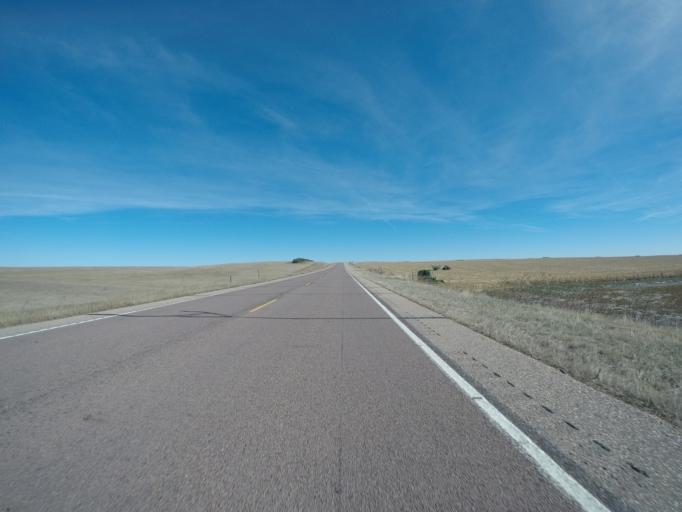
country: US
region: Colorado
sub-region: Kit Carson County
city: Burlington
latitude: 39.6579
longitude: -102.5106
